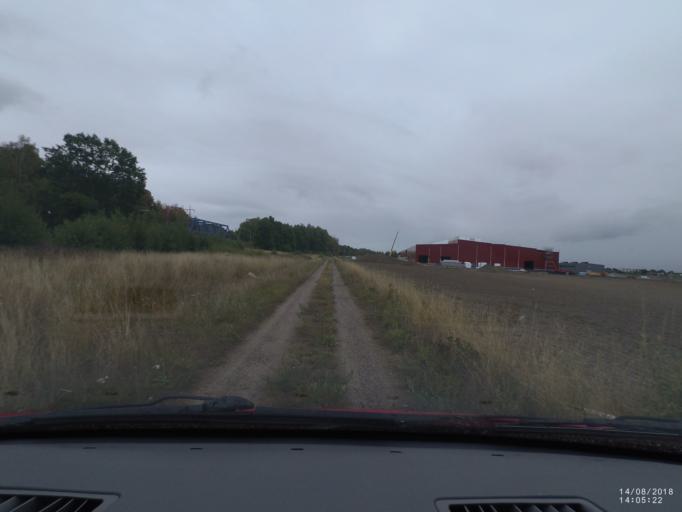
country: SE
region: Soedermanland
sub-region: Nykopings Kommun
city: Nykoping
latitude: 58.7574
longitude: 16.9675
